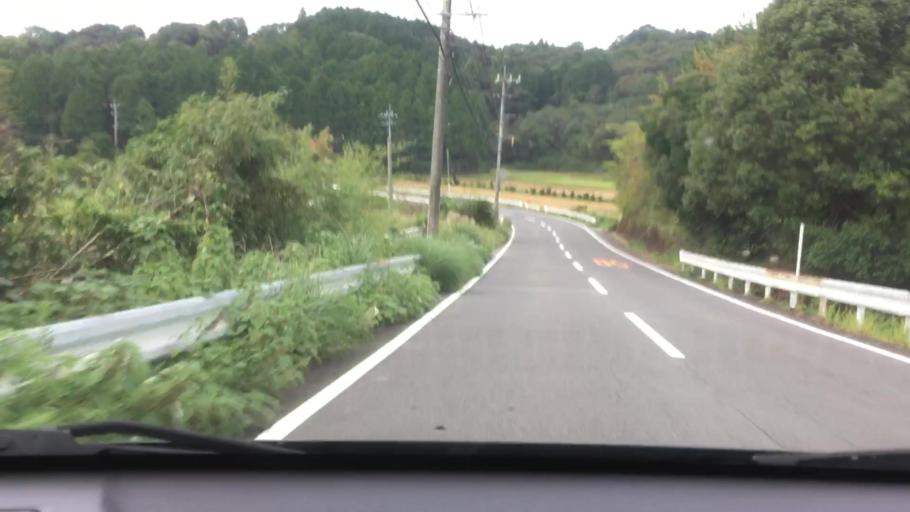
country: JP
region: Nagasaki
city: Sasebo
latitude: 32.9559
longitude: 129.6767
